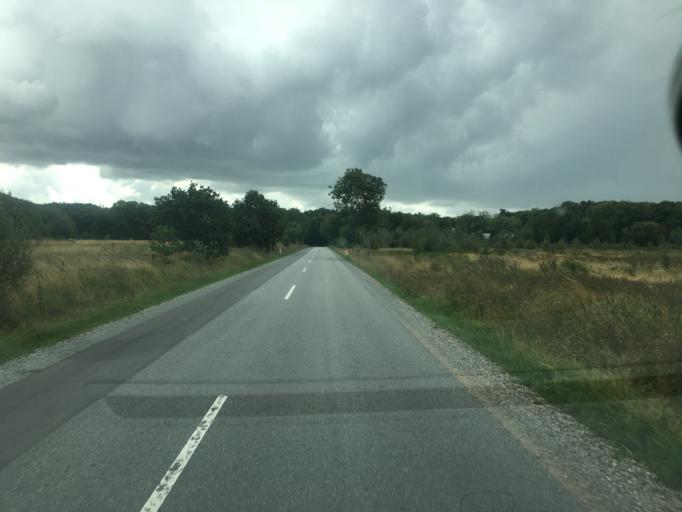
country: DK
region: South Denmark
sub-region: Tonder Kommune
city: Logumkloster
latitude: 55.0194
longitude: 8.9675
